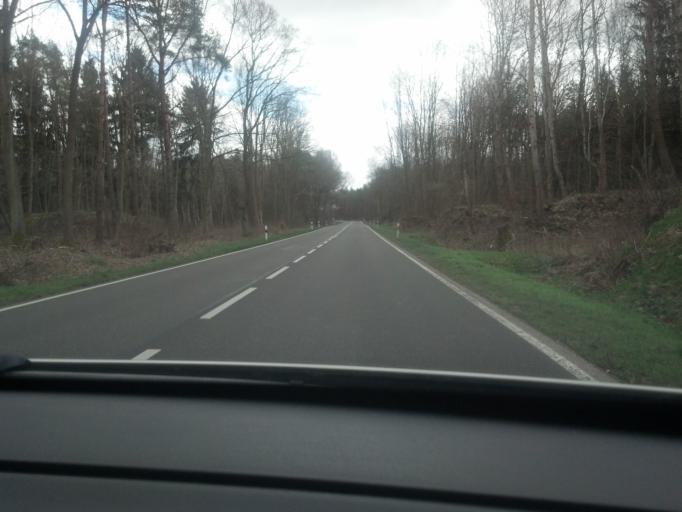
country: DE
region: Mecklenburg-Vorpommern
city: Rechlin
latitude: 53.3014
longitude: 12.7775
